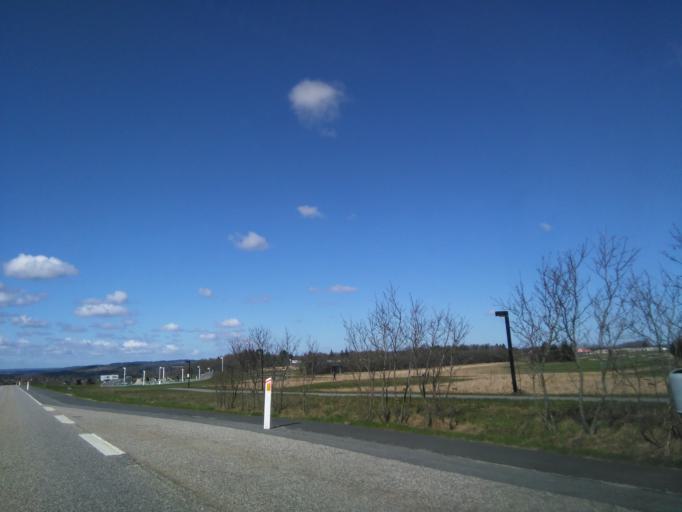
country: DK
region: Central Jutland
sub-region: Skanderborg Kommune
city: Ry
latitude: 56.0870
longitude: 9.7950
